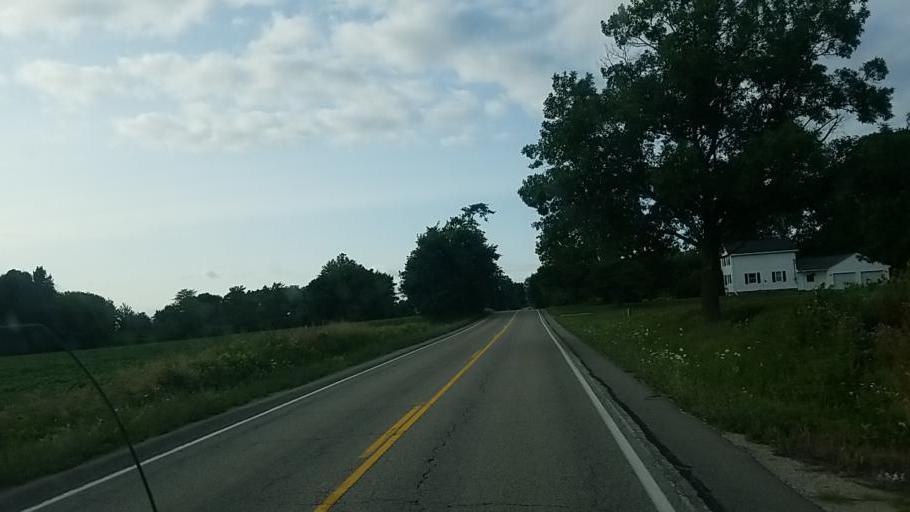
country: US
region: Michigan
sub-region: Ionia County
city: Belding
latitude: 43.1020
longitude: -85.3525
